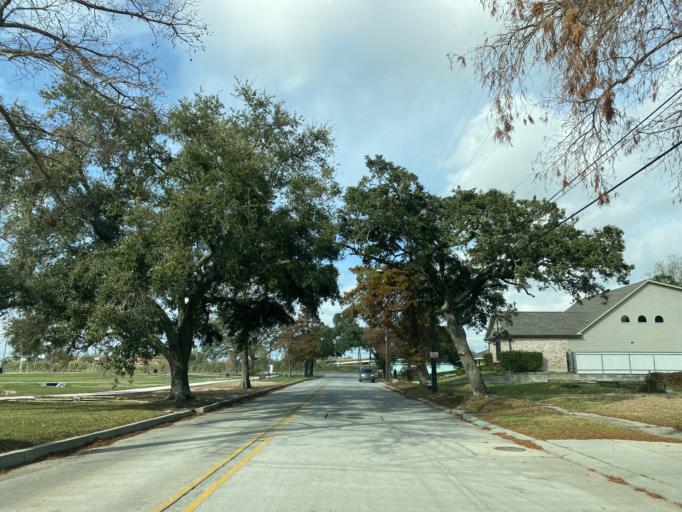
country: US
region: Louisiana
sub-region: Saint Bernard Parish
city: Arabi
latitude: 30.0285
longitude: -90.0384
